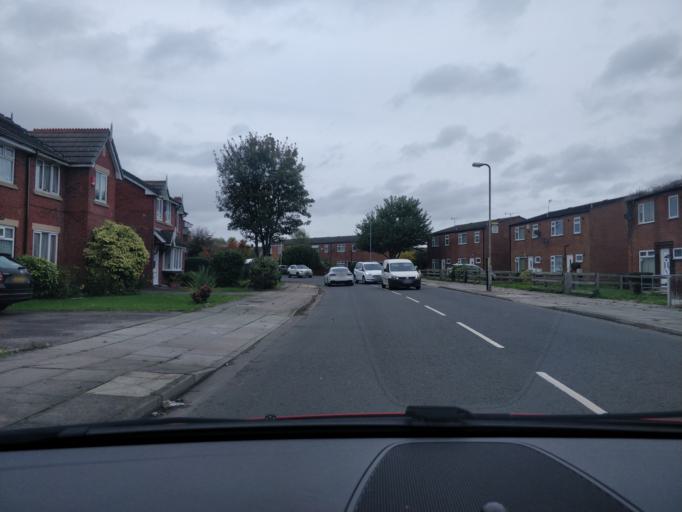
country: GB
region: England
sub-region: Sefton
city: Southport
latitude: 53.6338
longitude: -2.9864
